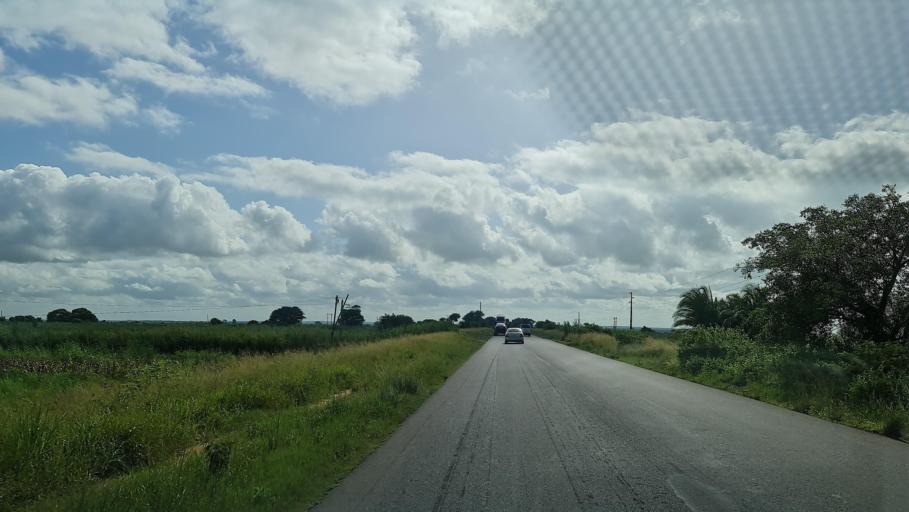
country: MZ
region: Gaza
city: Macia
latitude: -25.0795
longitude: 32.8894
